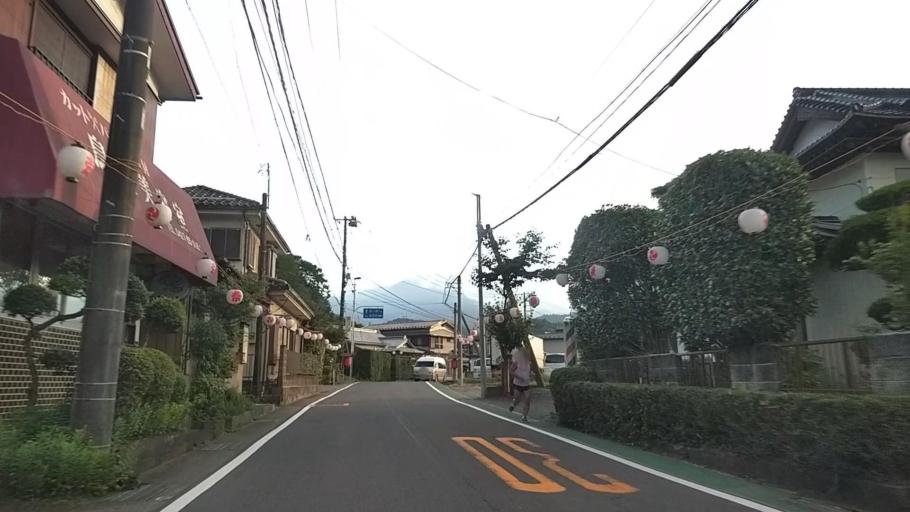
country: JP
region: Yamanashi
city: Uenohara
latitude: 35.5477
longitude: 139.2220
